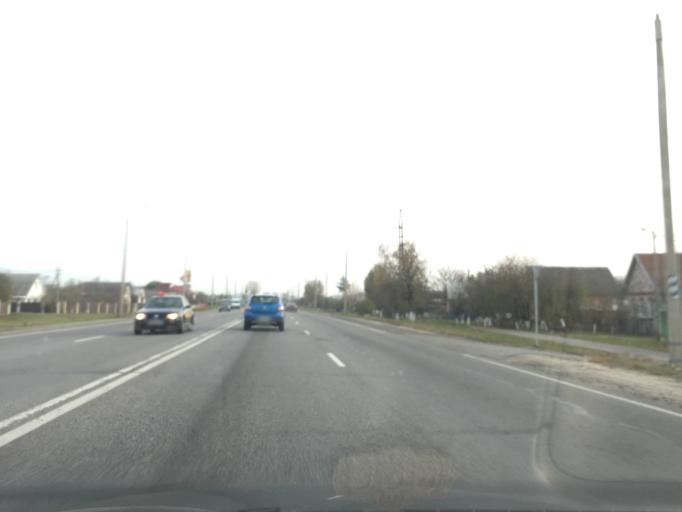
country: BY
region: Gomel
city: Gomel
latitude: 52.4928
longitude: 30.9617
